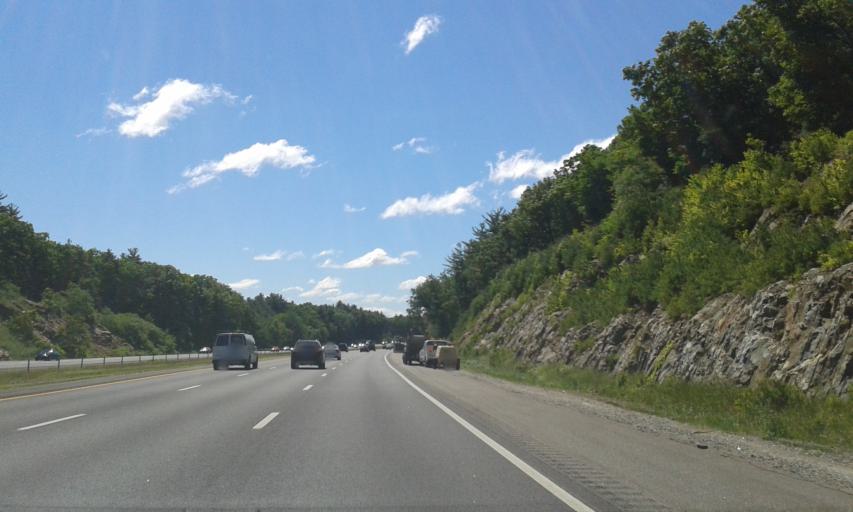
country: US
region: Massachusetts
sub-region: Middlesex County
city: Billerica
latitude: 42.5258
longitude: -71.2685
